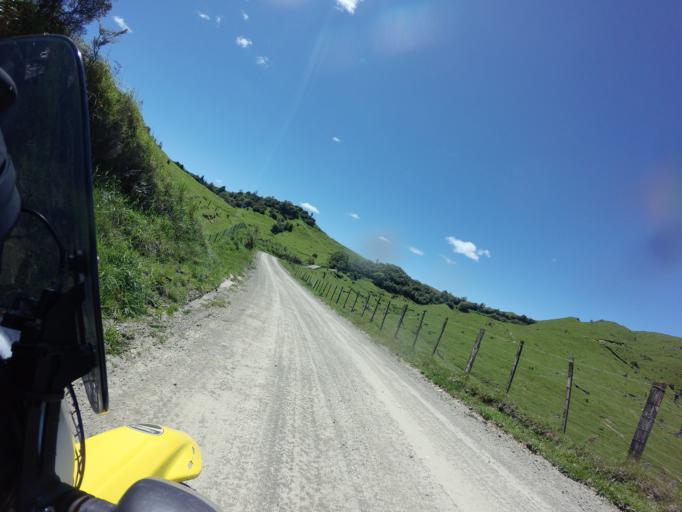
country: NZ
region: Bay of Plenty
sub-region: Opotiki District
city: Opotiki
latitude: -38.4086
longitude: 177.4410
